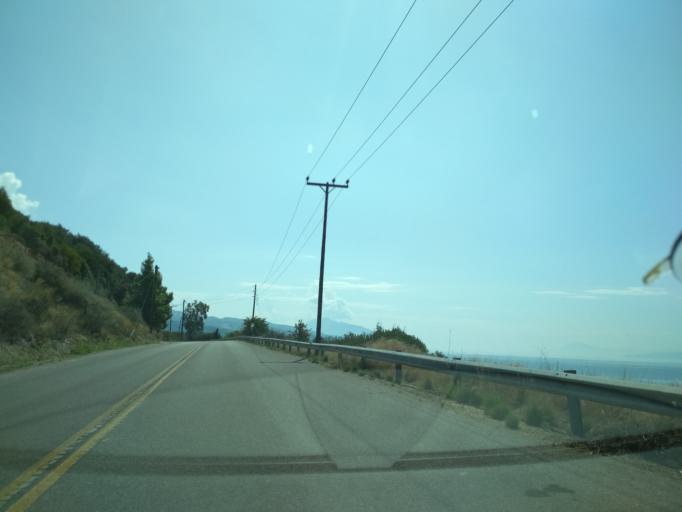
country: GR
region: Central Greece
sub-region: Nomos Evvoias
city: Roviai
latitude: 38.8385
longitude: 23.1792
